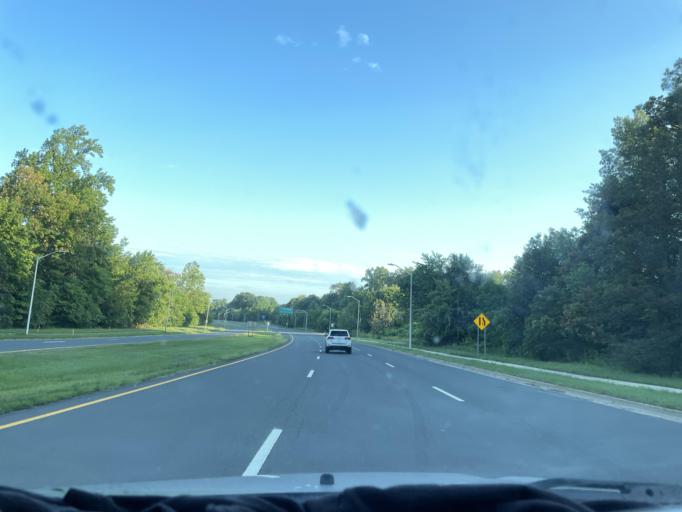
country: US
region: Maryland
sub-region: Montgomery County
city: Gaithersburg
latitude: 39.1048
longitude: -77.2069
